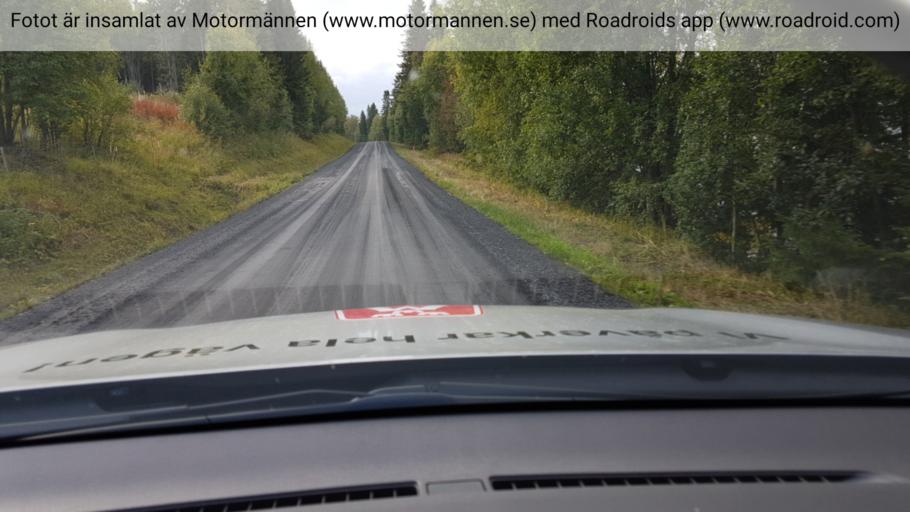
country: SE
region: Jaemtland
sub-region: Stroemsunds Kommun
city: Stroemsund
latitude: 64.1430
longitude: 15.7096
